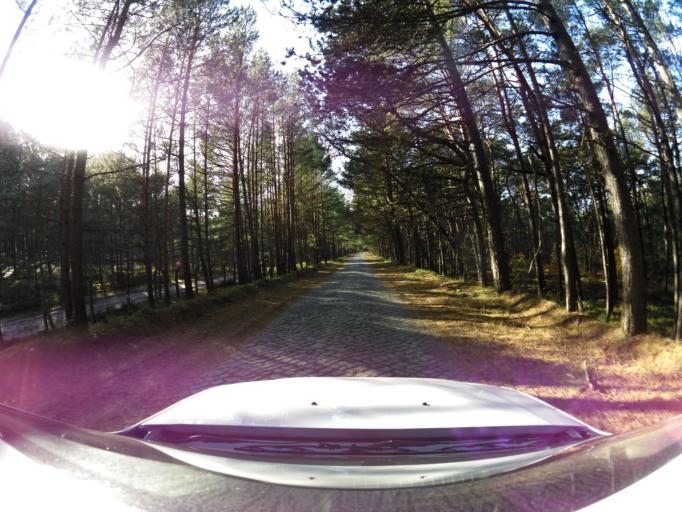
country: PL
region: West Pomeranian Voivodeship
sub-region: Powiat gryficki
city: Trzebiatow
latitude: 54.1179
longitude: 15.1781
